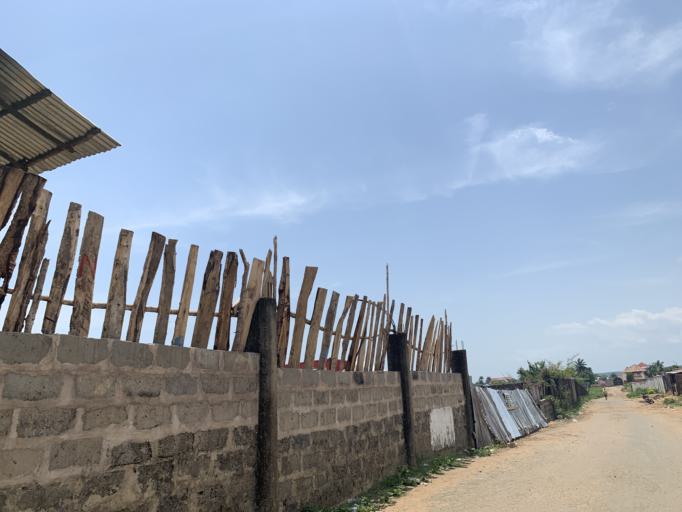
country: SL
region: Western Area
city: Waterloo
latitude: 8.3383
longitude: -13.0325
